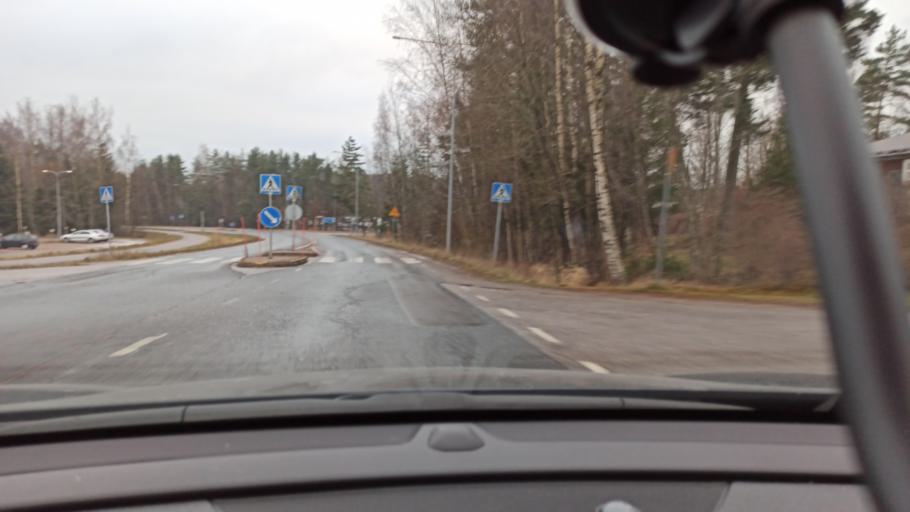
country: FI
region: Uusimaa
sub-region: Helsinki
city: Kirkkonummi
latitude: 60.1353
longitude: 24.4452
